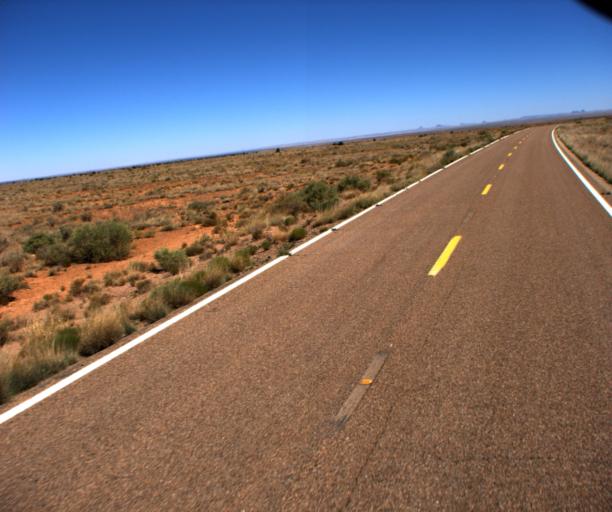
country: US
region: Arizona
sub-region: Navajo County
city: Winslow
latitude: 34.8975
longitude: -110.6448
